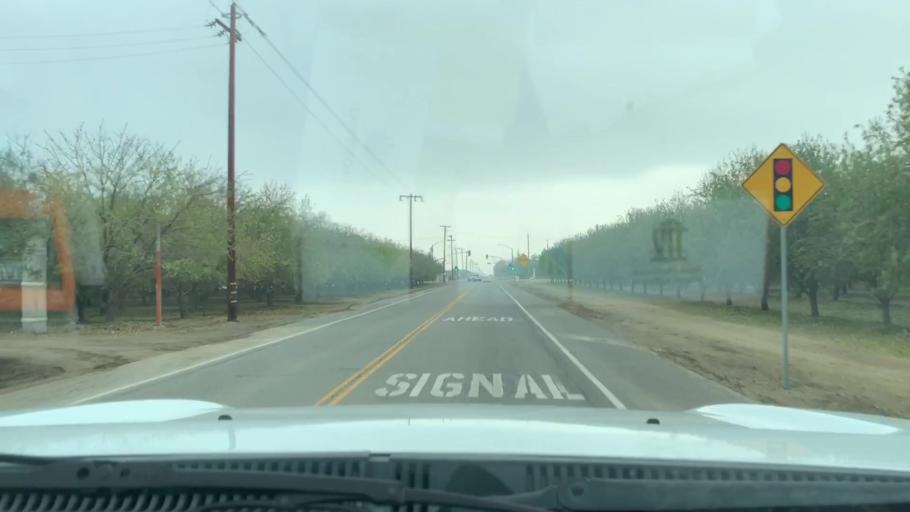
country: US
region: California
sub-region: Kern County
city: Wasco
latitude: 35.5579
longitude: -119.3346
